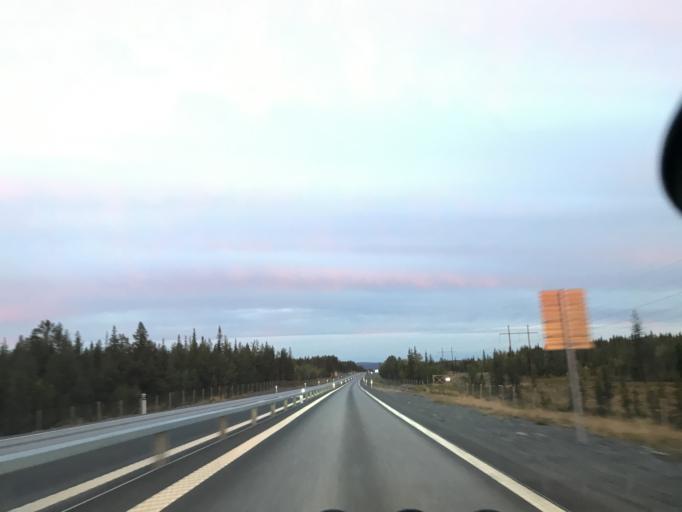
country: SE
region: Norrbotten
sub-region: Gallivare Kommun
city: Malmberget
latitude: 67.6867
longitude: 20.8524
